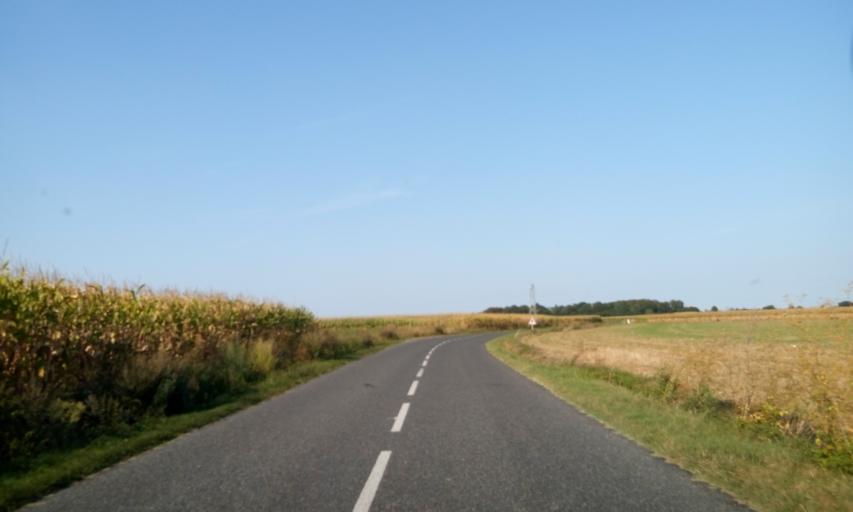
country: FR
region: Rhone-Alpes
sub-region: Departement de l'Ain
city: Sainte-Euphemie
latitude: 45.9707
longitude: 4.7800
